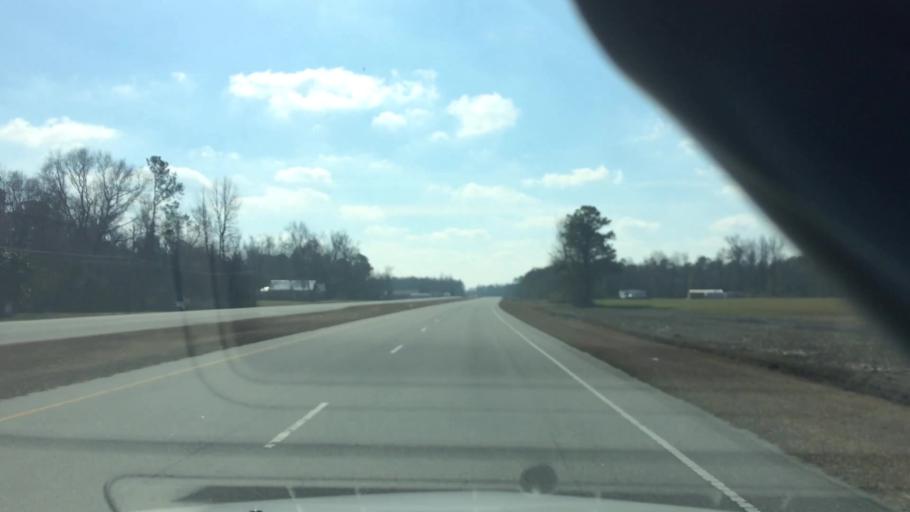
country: US
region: North Carolina
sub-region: Duplin County
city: Beulaville
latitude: 35.0945
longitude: -77.7263
